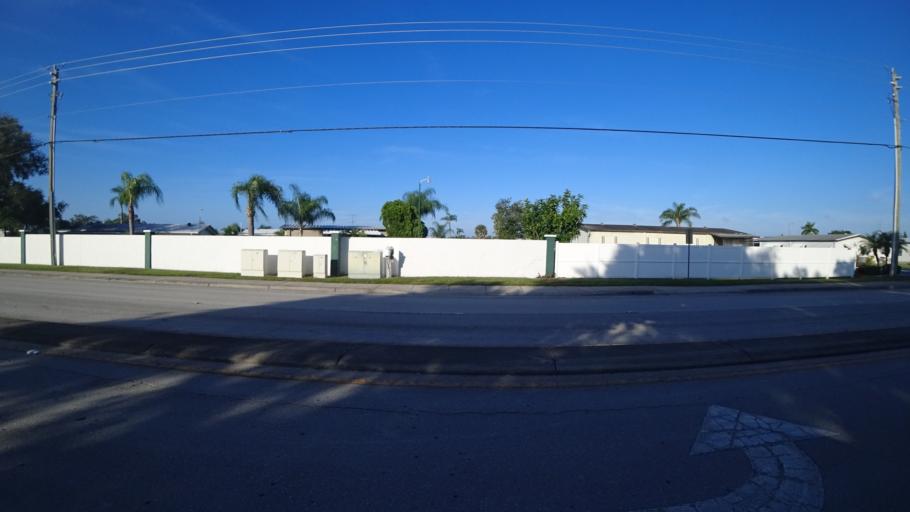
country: US
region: Florida
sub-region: Manatee County
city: West Samoset
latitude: 27.4585
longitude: -82.5548
